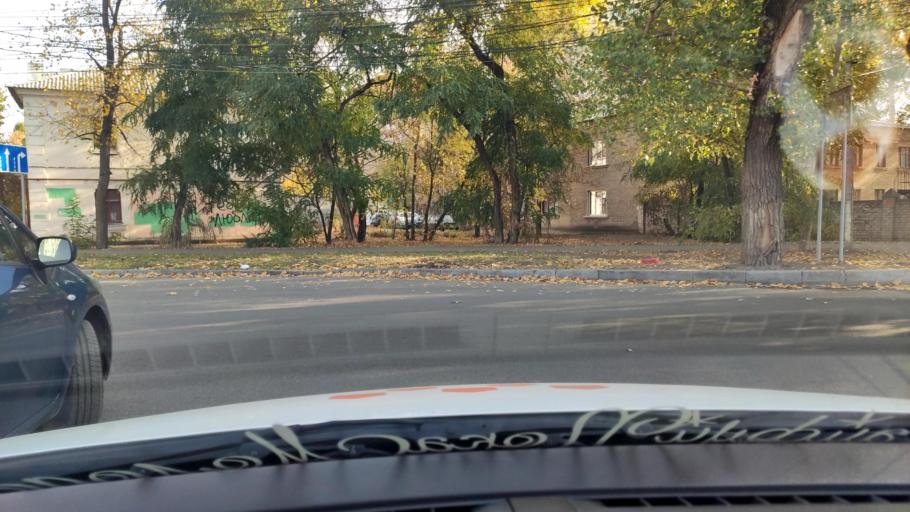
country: RU
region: Voronezj
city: Voronezh
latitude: 51.6987
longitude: 39.1964
